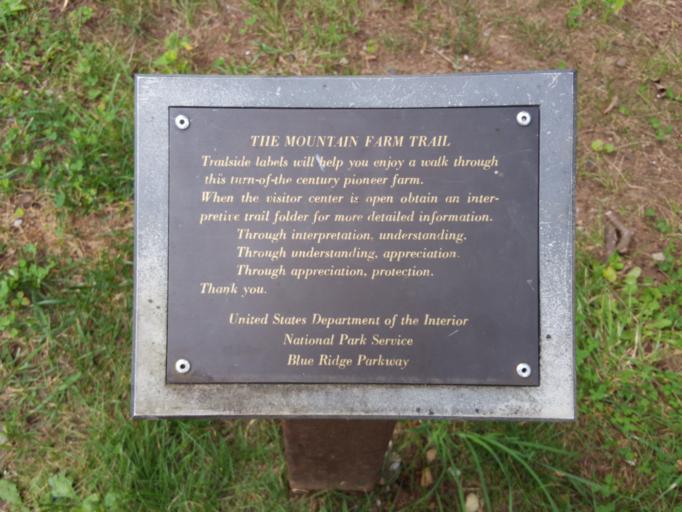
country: US
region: Virginia
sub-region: Augusta County
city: Lyndhurst
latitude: 37.9723
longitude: -78.8993
